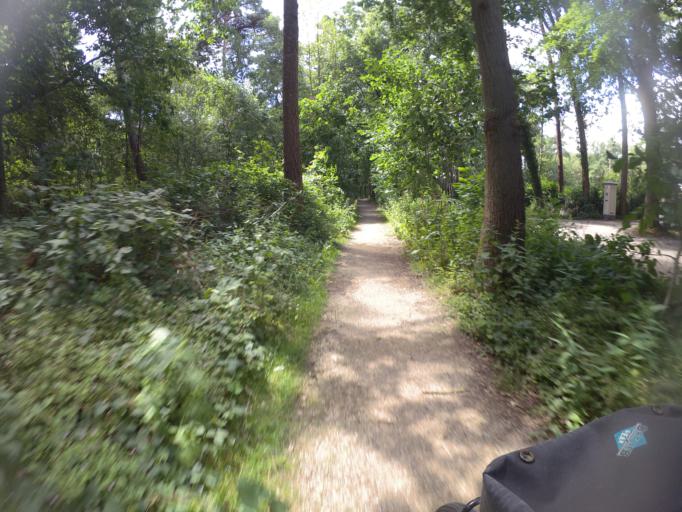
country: NL
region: North Brabant
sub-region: Gemeente Oisterwijk
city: Oisterwijk
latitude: 51.5711
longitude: 5.2084
